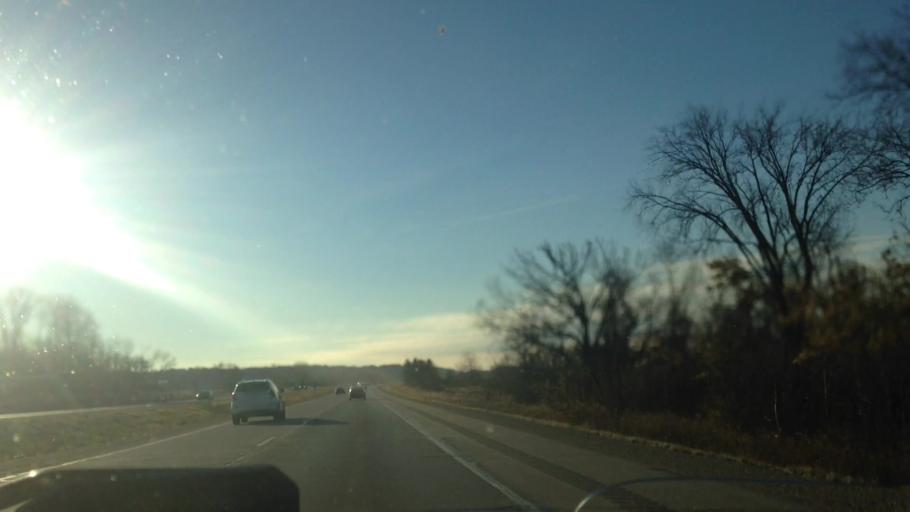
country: US
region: Wisconsin
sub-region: Washington County
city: Slinger
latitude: 43.3926
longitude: -88.3147
